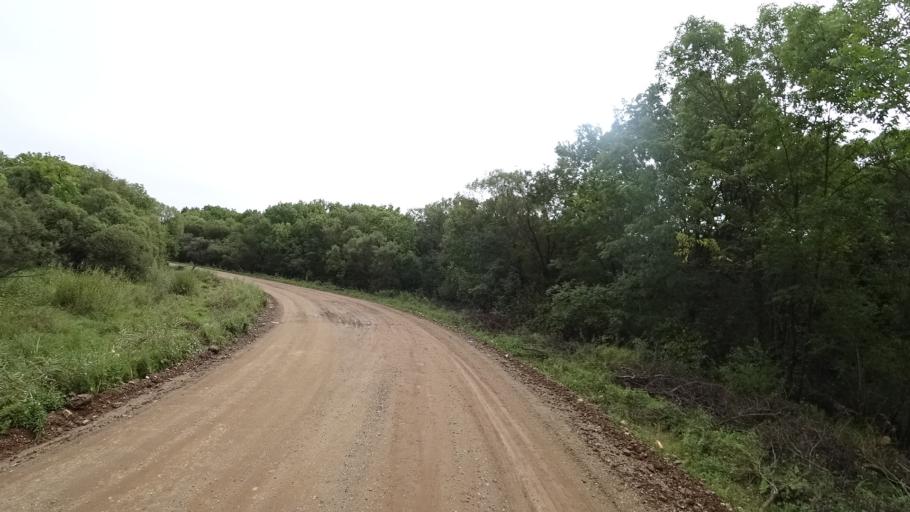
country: RU
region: Primorskiy
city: Lyalichi
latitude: 44.0794
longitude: 132.4508
